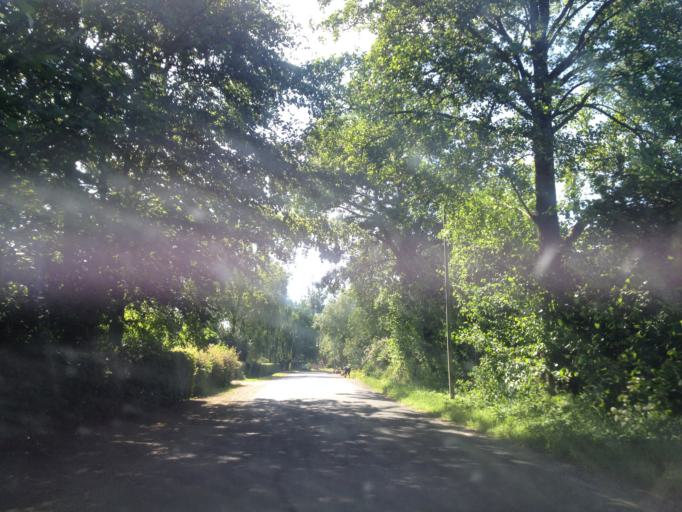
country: DK
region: South Denmark
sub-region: Kolding Kommune
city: Christiansfeld
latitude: 55.4009
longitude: 9.5199
